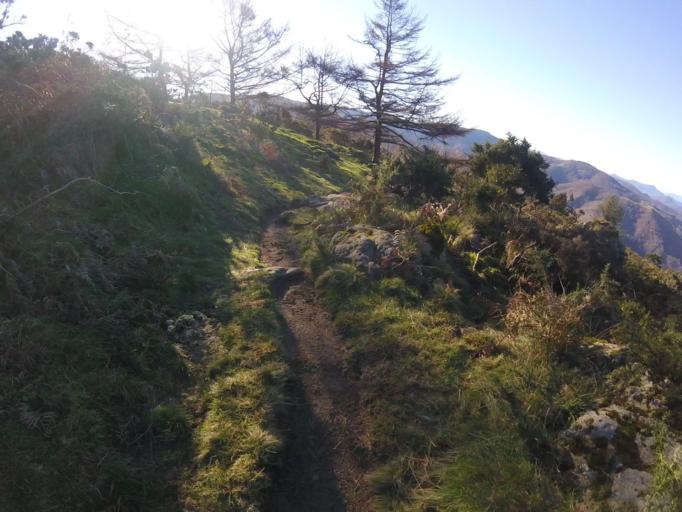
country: ES
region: Basque Country
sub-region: Provincia de Guipuzcoa
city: Irun
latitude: 43.2759
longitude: -1.7974
